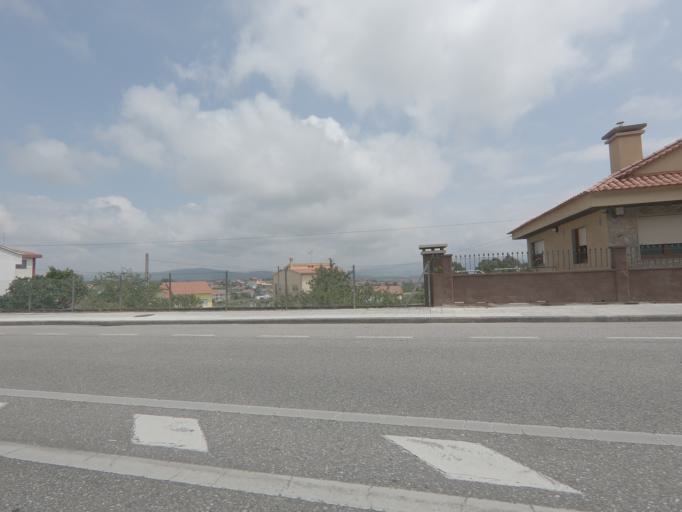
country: ES
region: Galicia
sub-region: Provincia de Pontevedra
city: A Guarda
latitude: 41.9024
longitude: -8.8642
